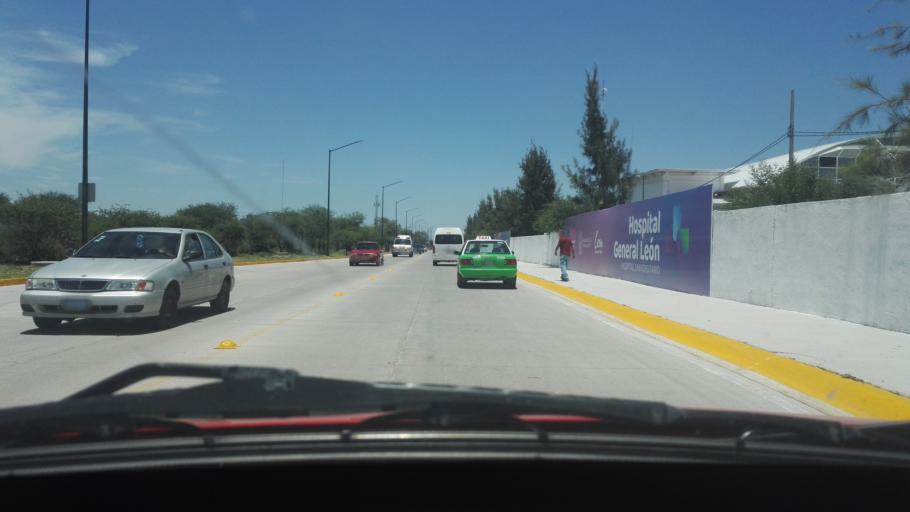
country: MX
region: Guanajuato
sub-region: Leon
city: Ladrilleras del Refugio
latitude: 21.0596
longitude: -101.5701
